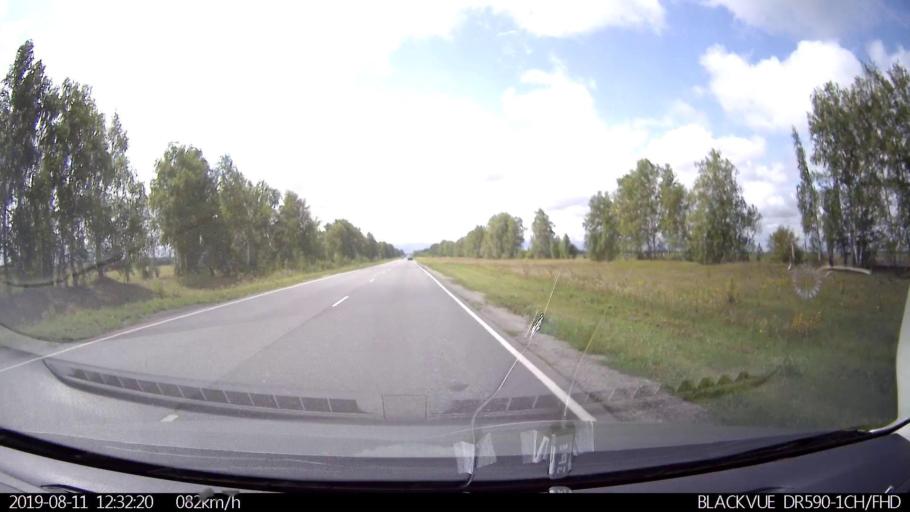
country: RU
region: Ulyanovsk
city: Ignatovka
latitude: 53.8148
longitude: 47.8706
